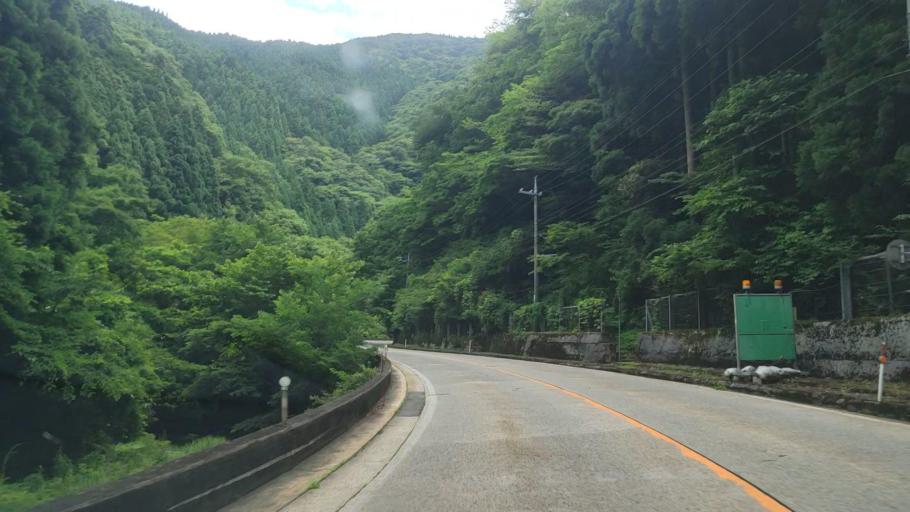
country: JP
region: Okayama
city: Niimi
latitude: 35.2135
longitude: 133.4803
